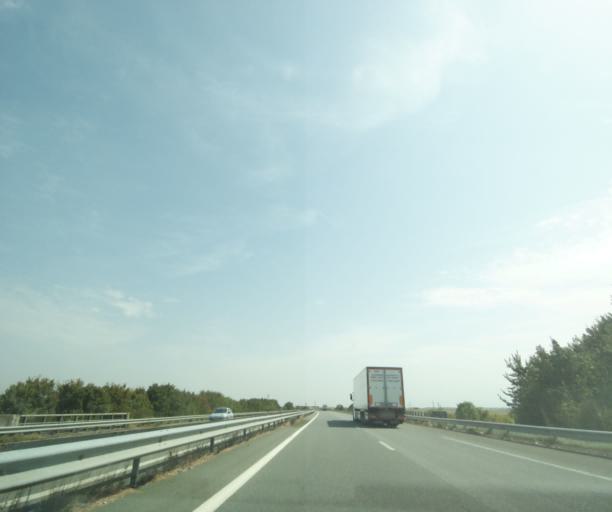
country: FR
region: Pays de la Loire
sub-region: Departement de la Vendee
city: Maillezais
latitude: 46.4202
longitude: -0.7704
